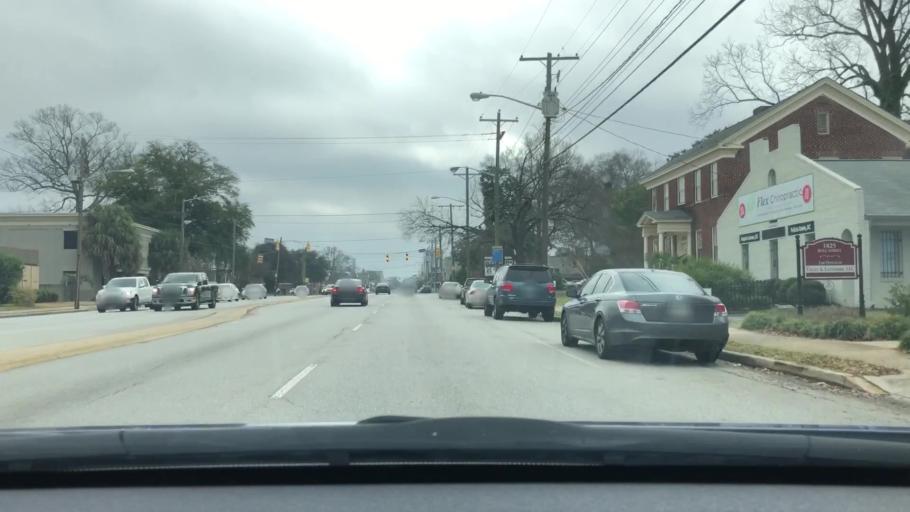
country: US
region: South Carolina
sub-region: Richland County
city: Columbia
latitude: 34.0116
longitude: -81.0328
